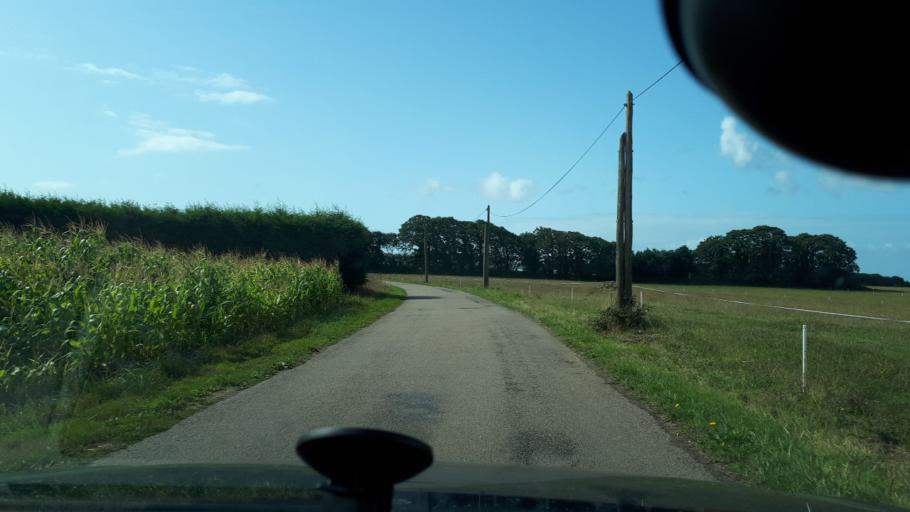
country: FR
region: Brittany
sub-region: Departement du Finistere
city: Pouldreuzic
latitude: 47.9830
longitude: -4.3697
